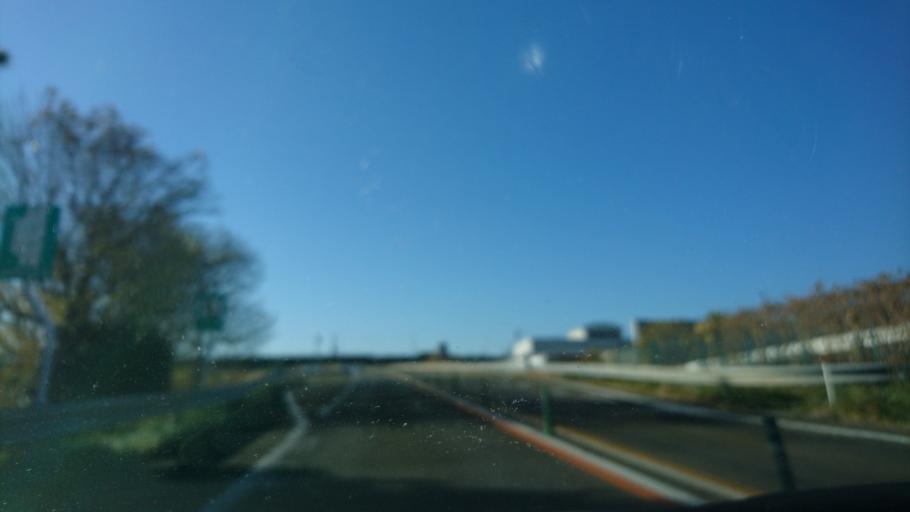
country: JP
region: Miyagi
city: Sendai
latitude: 38.2087
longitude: 140.8803
